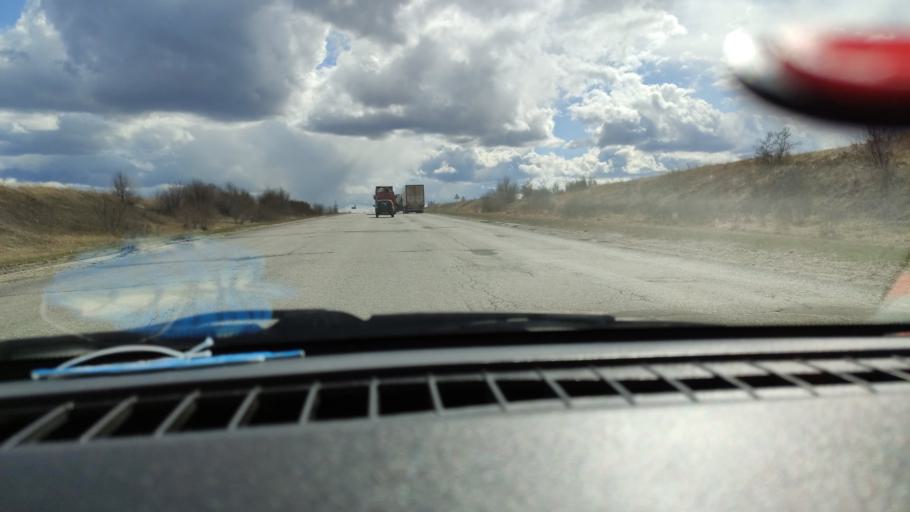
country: RU
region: Samara
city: Varlamovo
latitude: 53.0873
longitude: 48.3549
